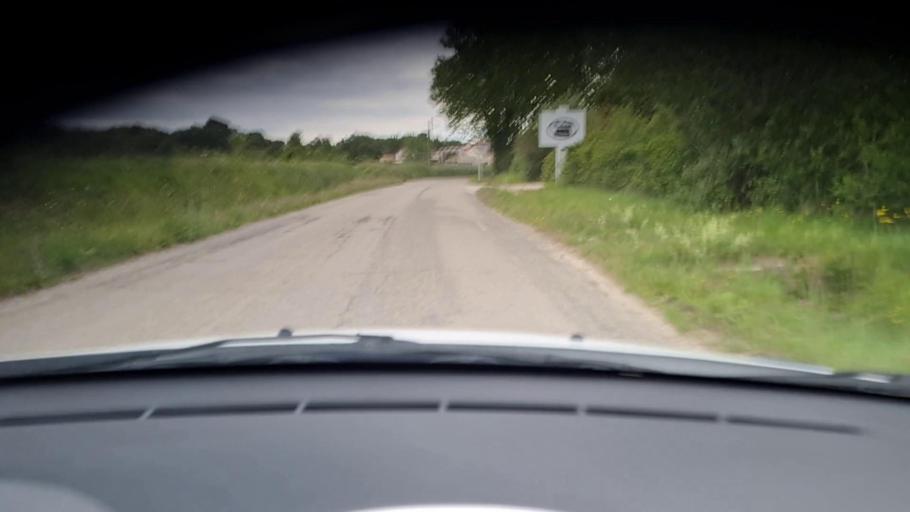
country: FR
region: Languedoc-Roussillon
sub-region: Departement du Gard
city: Castillon-du-Gard
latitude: 43.9668
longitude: 4.5136
